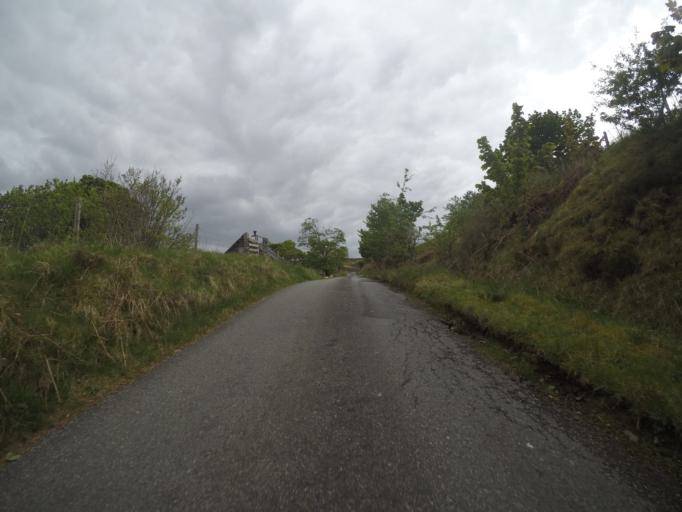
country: GB
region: Scotland
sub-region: Highland
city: Isle of Skye
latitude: 57.2990
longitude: -6.3580
